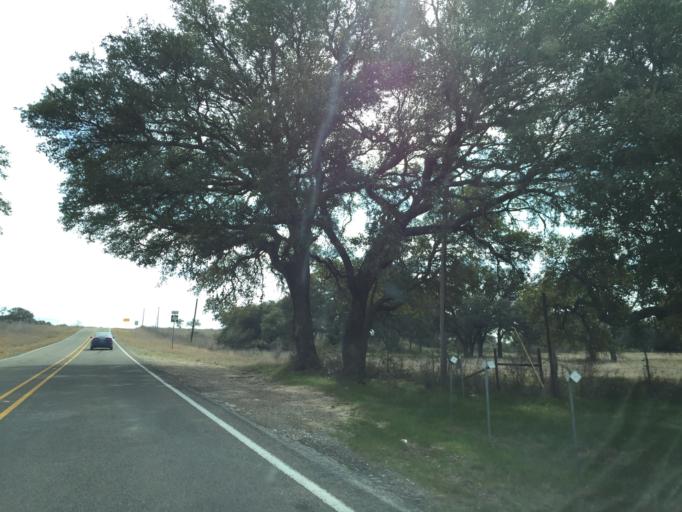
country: US
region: Texas
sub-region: Burnet County
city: Granite Shoals
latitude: 30.4972
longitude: -98.4396
